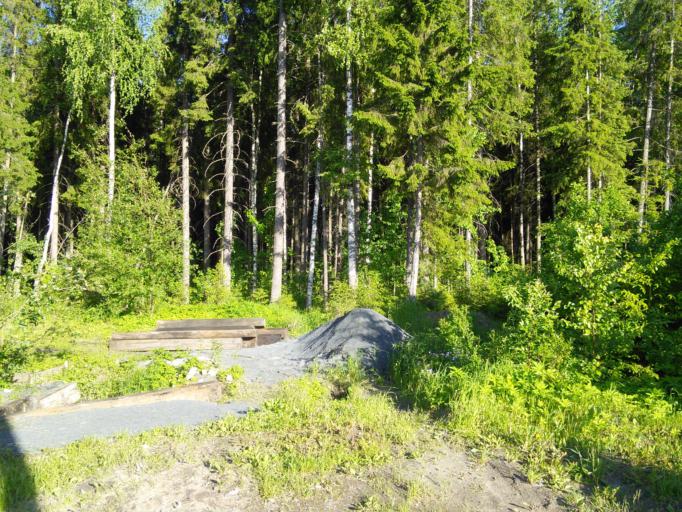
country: RU
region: Republic of Karelia
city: Shuya
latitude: 61.8489
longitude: 34.1423
